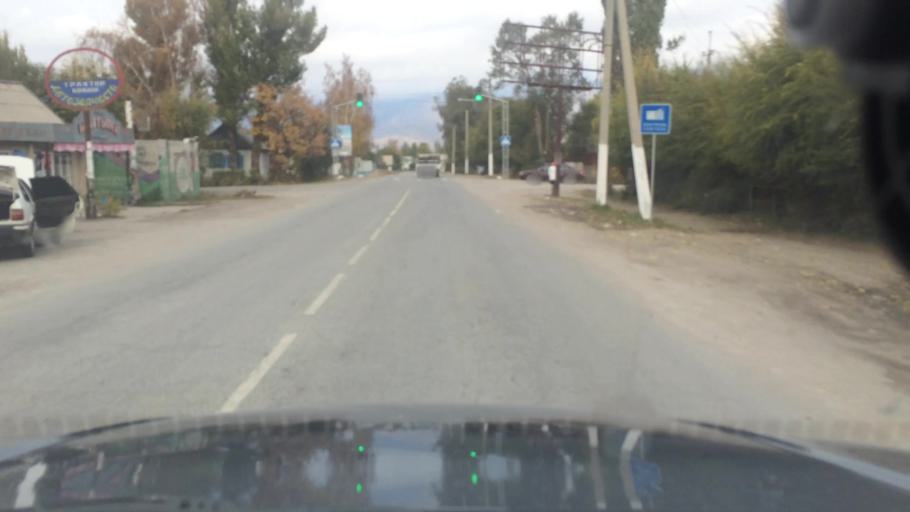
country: KG
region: Ysyk-Koel
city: Tyup
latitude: 42.7268
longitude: 78.3620
